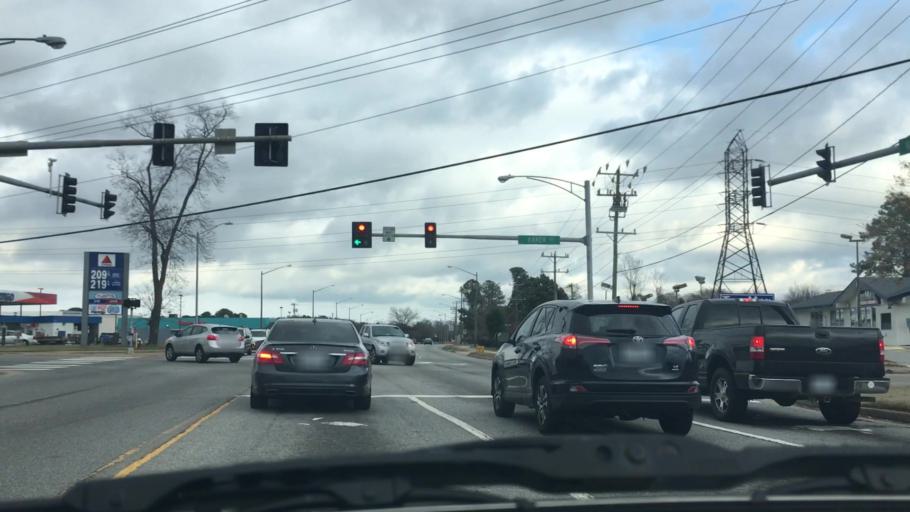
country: US
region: Virginia
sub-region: City of Chesapeake
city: Chesapeake
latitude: 36.8594
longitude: -76.1755
